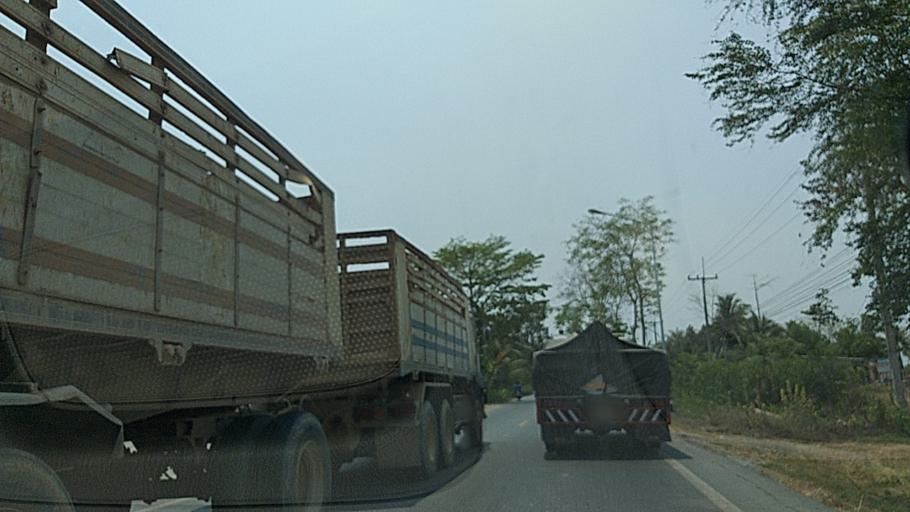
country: TH
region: Chachoengsao
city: Bang Nam Priao
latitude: 13.8969
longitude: 100.9716
